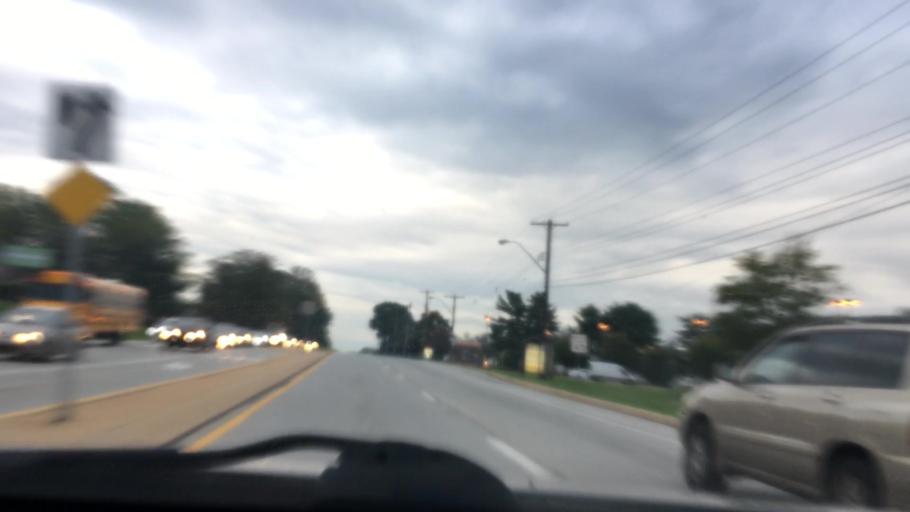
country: US
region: Pennsylvania
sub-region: Chester County
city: West Chester
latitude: 39.9677
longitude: -75.5548
